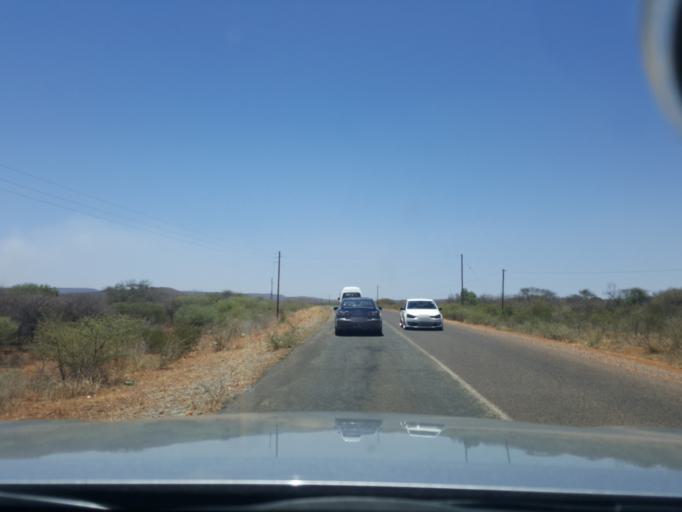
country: ZA
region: North-West
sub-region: Ngaka Modiri Molema District Municipality
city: Zeerust
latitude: -25.3905
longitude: 25.9358
